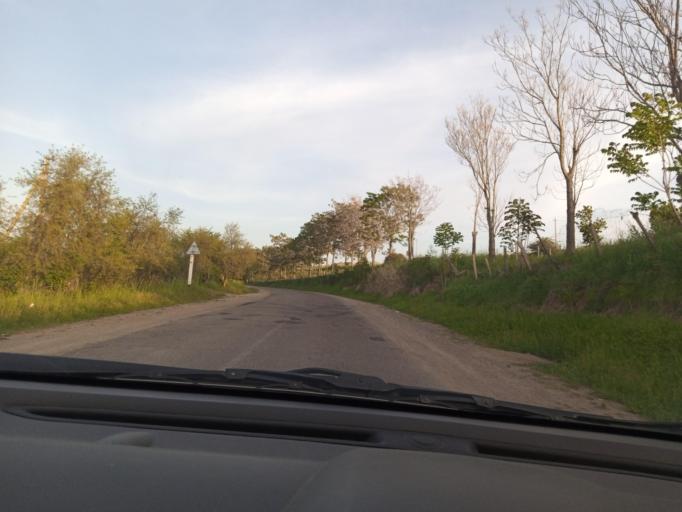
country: UZ
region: Toshkent
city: Parkent
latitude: 41.2382
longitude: 69.7340
